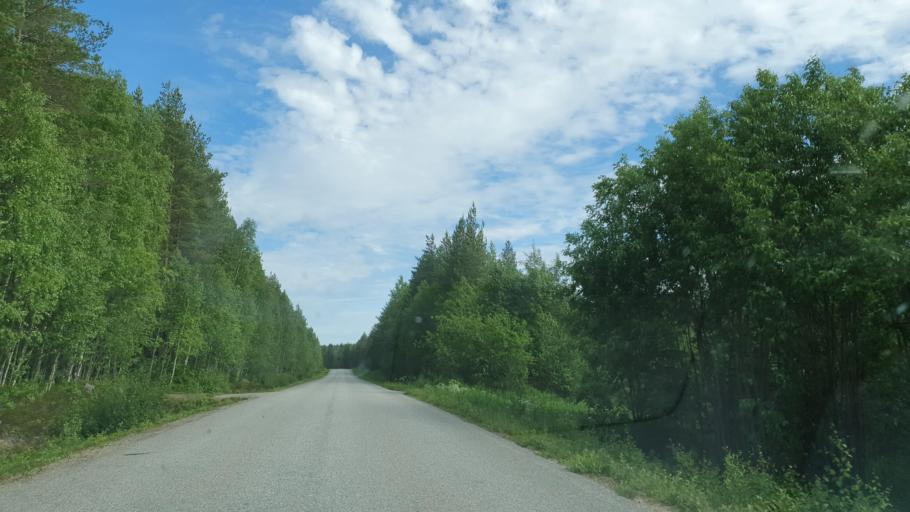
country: FI
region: Kainuu
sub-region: Kehys-Kainuu
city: Suomussalmi
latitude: 64.5540
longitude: 29.1686
